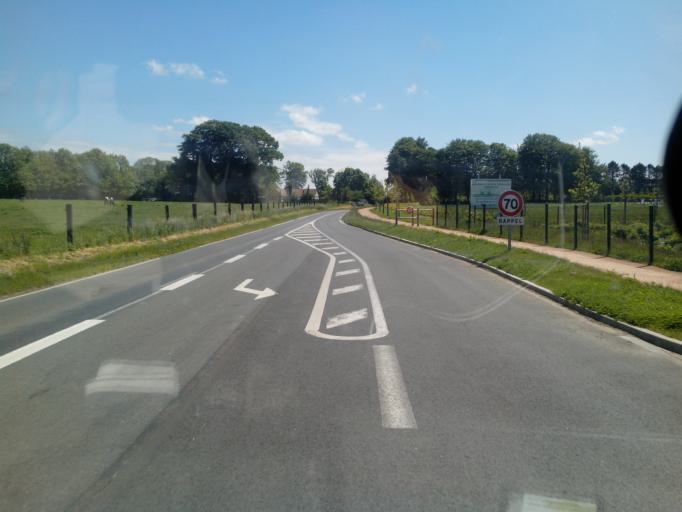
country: FR
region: Haute-Normandie
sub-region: Departement de la Seine-Maritime
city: Turretot
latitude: 49.6359
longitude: 0.2702
